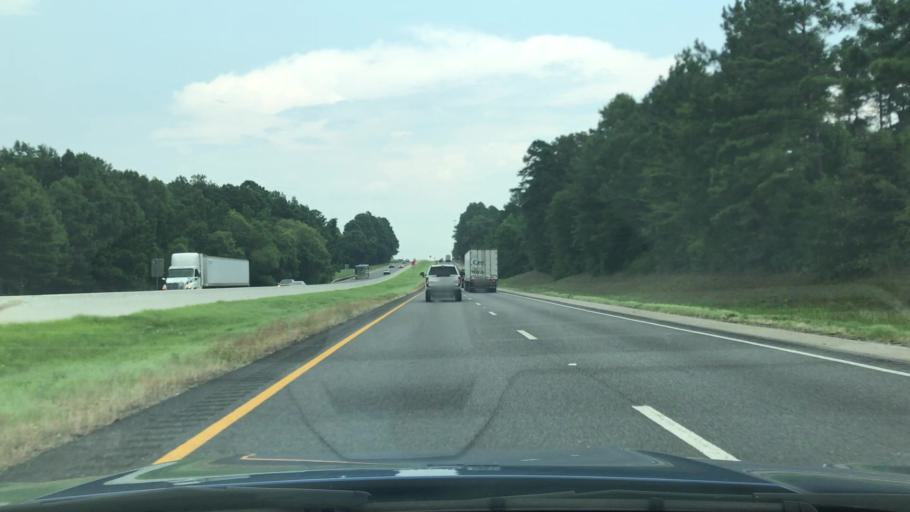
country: US
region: Texas
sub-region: Gregg County
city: Liberty City
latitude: 32.4351
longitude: -94.9580
